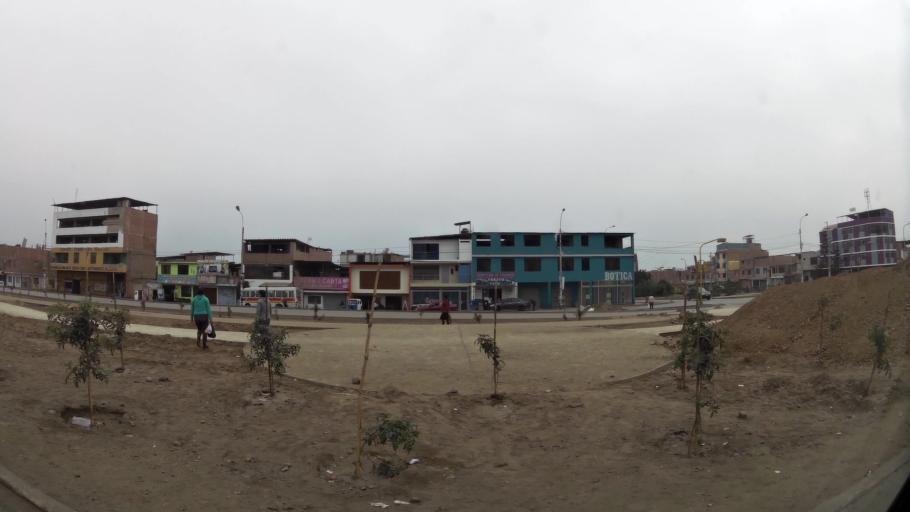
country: PE
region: Lima
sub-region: Lima
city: Surco
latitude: -12.2136
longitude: -76.9482
